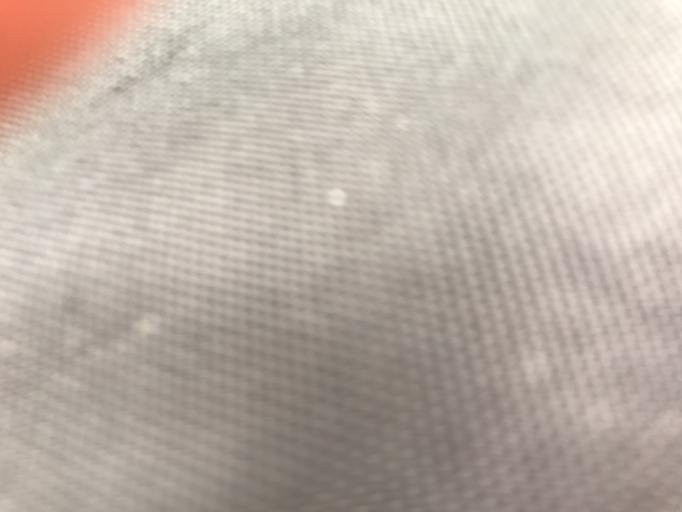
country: TN
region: Zaghwan
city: El Fahs
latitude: 36.2632
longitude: 9.7861
